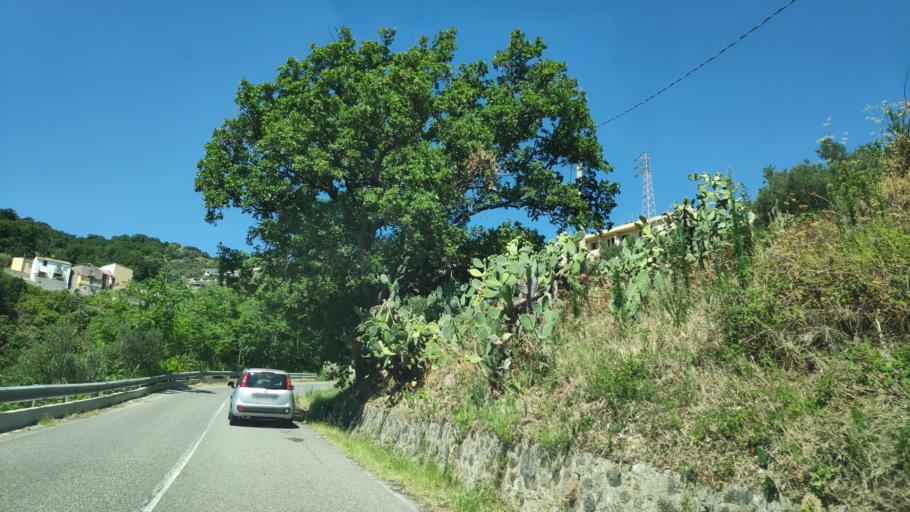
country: IT
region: Calabria
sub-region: Provincia di Catanzaro
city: Montauro
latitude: 38.7469
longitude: 16.5146
